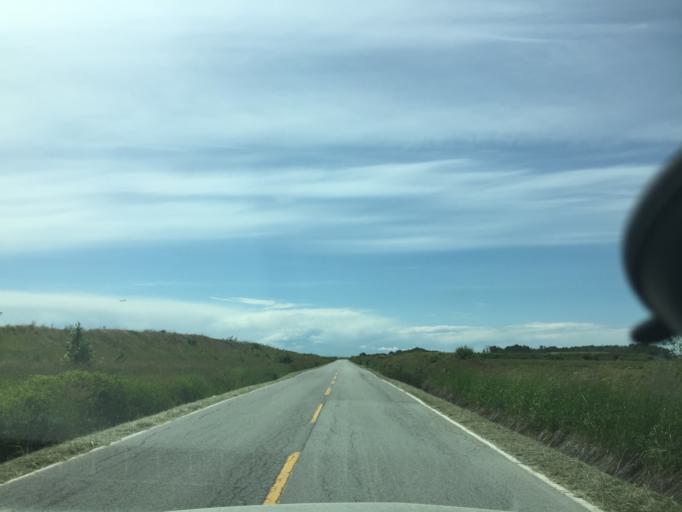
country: CA
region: British Columbia
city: Richmond
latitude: 49.2067
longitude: -123.1820
